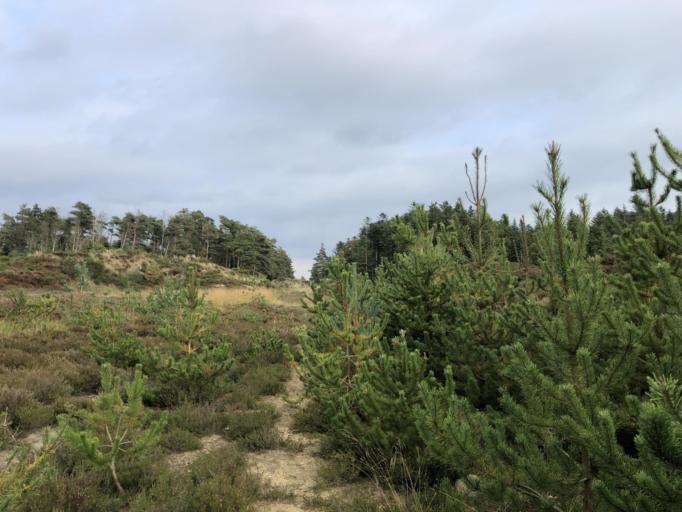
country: DK
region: Central Jutland
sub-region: Holstebro Kommune
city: Ulfborg
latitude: 56.2130
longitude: 8.4355
